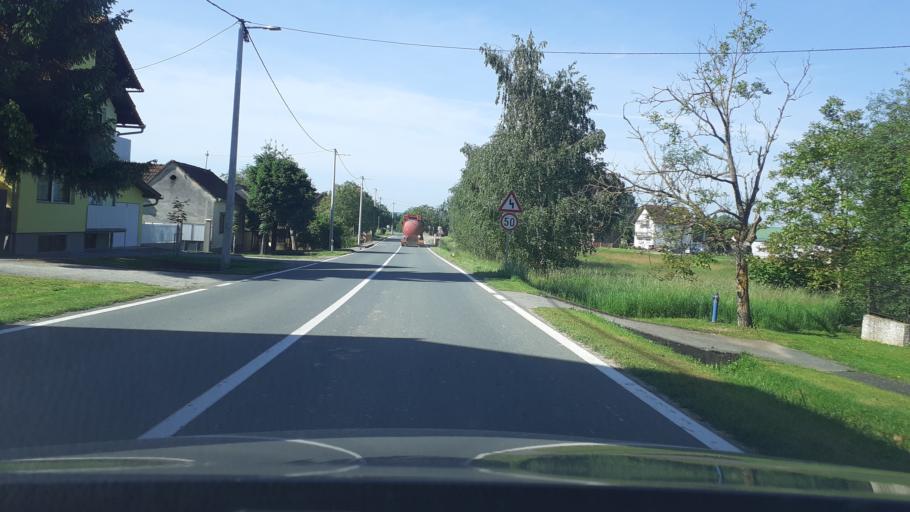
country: HR
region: Brodsko-Posavska
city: Batrina
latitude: 45.1958
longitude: 17.6635
